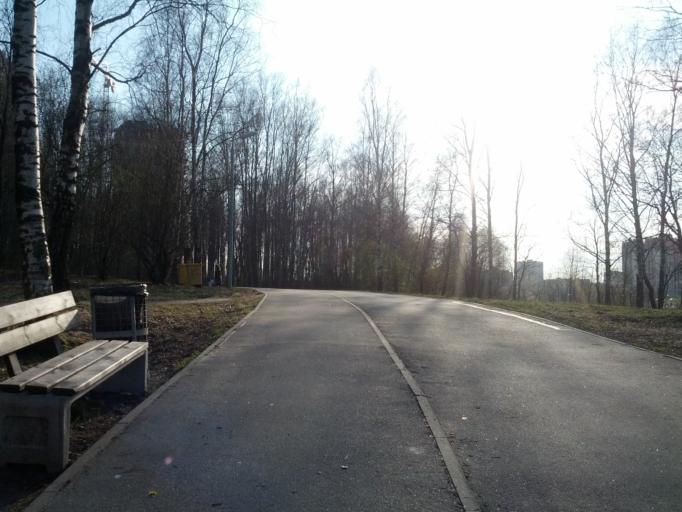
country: RU
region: St.-Petersburg
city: Krasnogvargeisky
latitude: 59.9122
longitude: 30.5187
